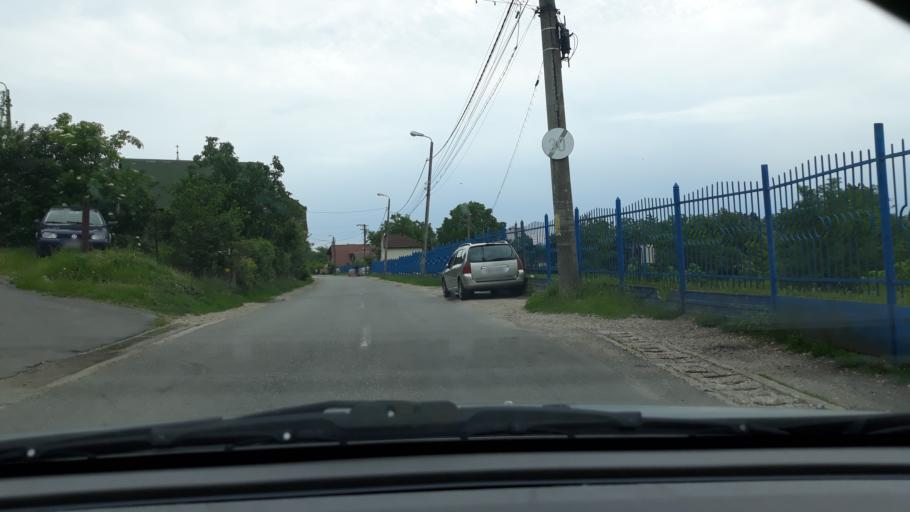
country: RO
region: Bihor
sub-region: Comuna Biharea
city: Oradea
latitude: 47.0525
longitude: 21.9632
